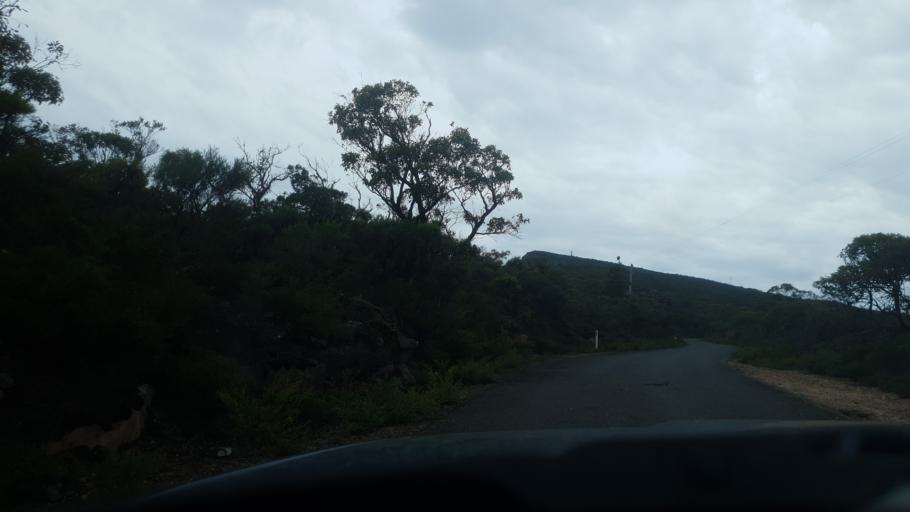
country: AU
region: Victoria
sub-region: Northern Grampians
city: Stawell
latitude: -37.2801
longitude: 142.5854
